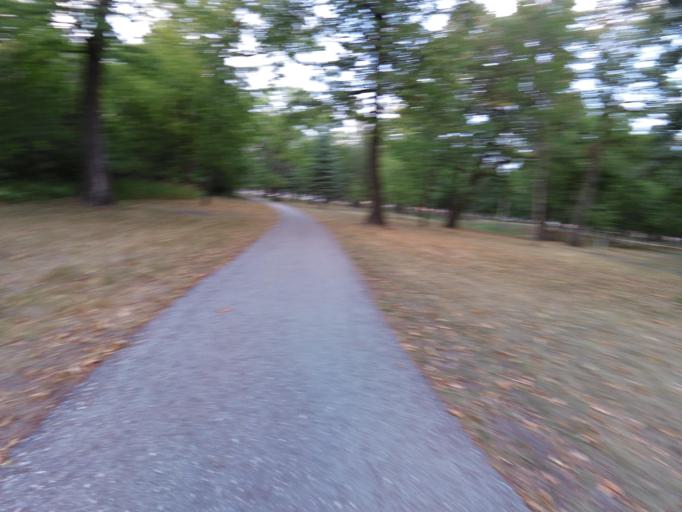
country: CA
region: Manitoba
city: Portage la Prairie
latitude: 49.9629
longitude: -98.2886
